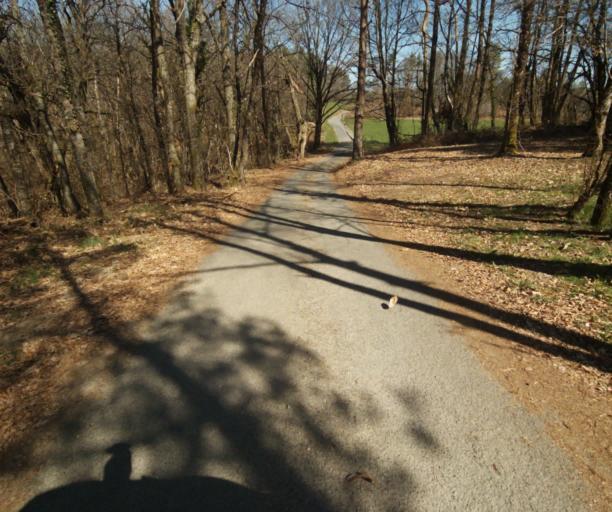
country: FR
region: Limousin
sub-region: Departement de la Correze
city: Saint-Mexant
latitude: 45.3033
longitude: 1.6380
